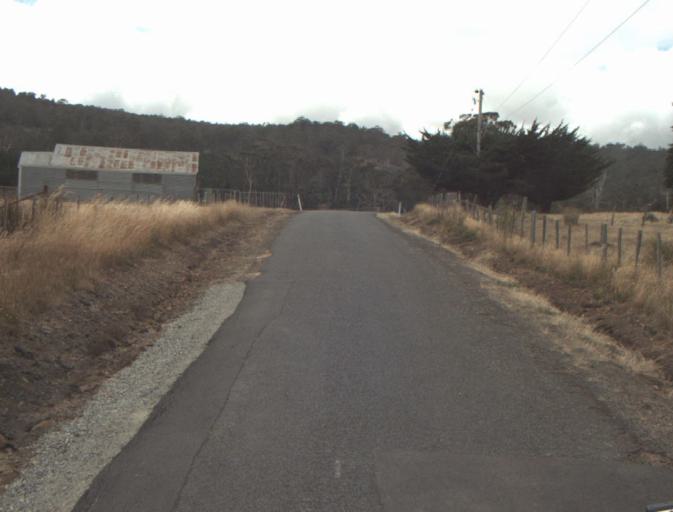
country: AU
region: Tasmania
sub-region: Northern Midlands
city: Evandale
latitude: -41.5214
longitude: 147.3936
